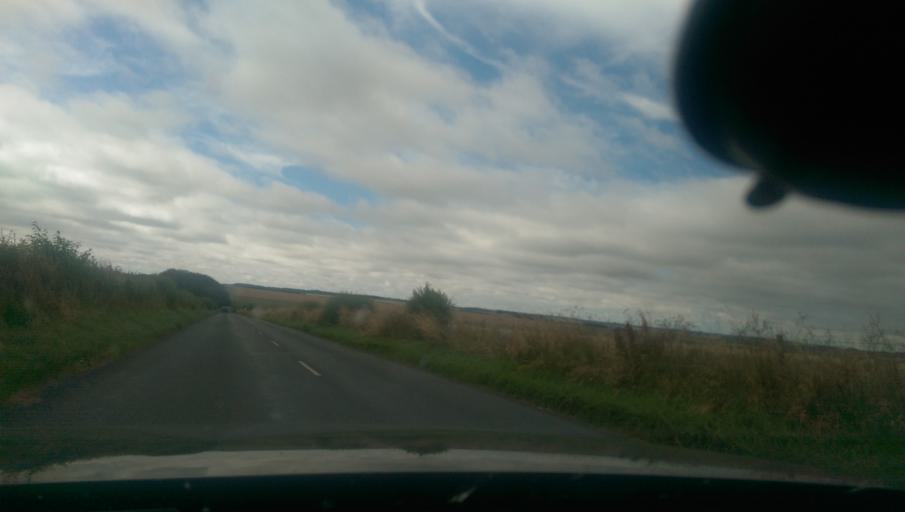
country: GB
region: England
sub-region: Wiltshire
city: Shrewton
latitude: 51.1965
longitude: -1.8621
